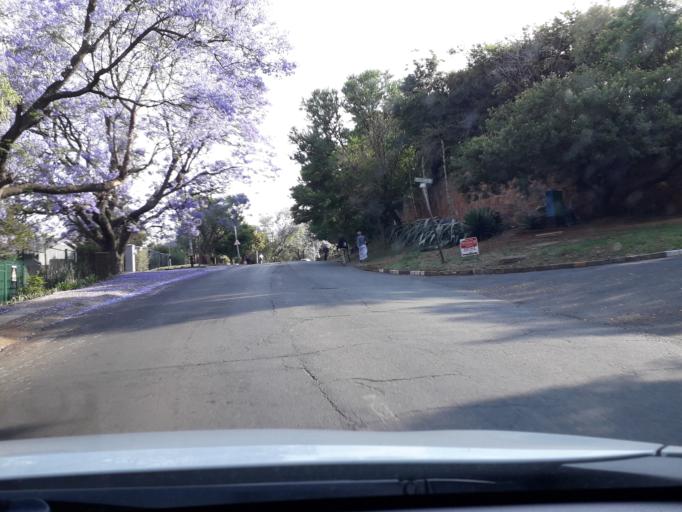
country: ZA
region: Gauteng
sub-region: City of Johannesburg Metropolitan Municipality
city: Roodepoort
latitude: -26.1474
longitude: 27.9577
